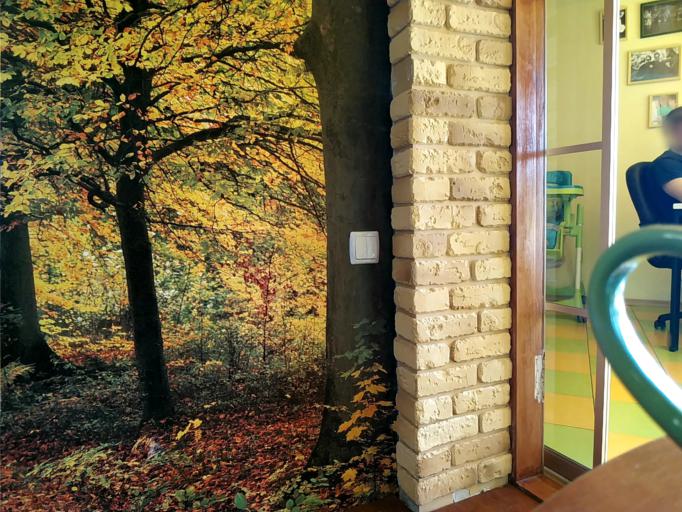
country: RU
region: Moskovskaya
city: Krasnoarmeysk
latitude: 56.0725
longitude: 38.2453
